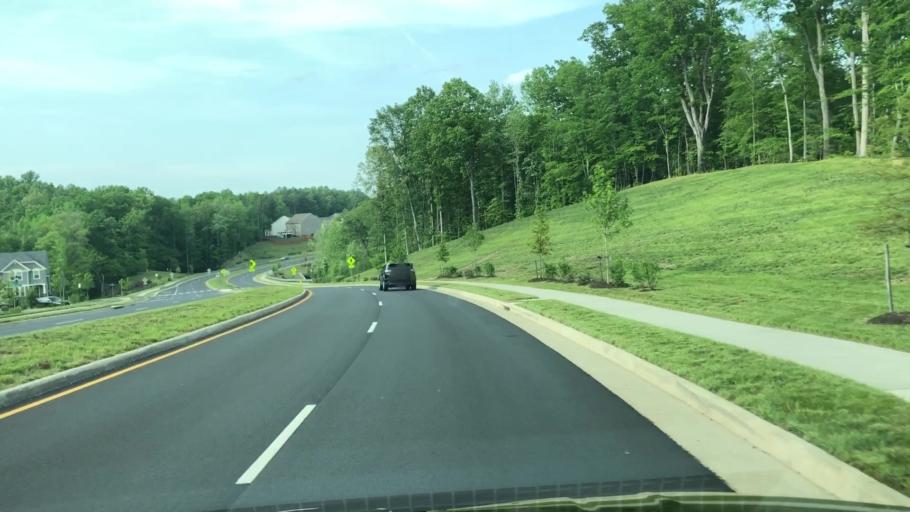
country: US
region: Virginia
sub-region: Stafford County
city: Stafford
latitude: 38.4295
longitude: -77.4614
